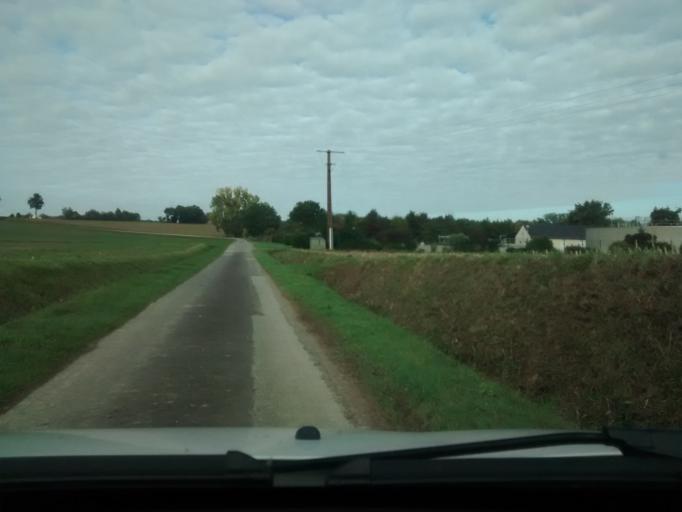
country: FR
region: Brittany
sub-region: Departement d'Ille-et-Vilaine
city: Chavagne
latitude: 48.0789
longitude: -1.7631
